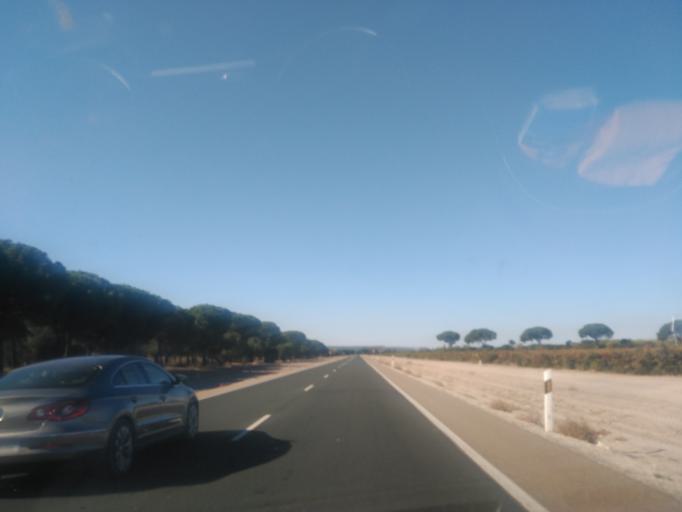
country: ES
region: Castille and Leon
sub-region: Provincia de Valladolid
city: Sardon de Duero
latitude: 41.6141
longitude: -4.4035
